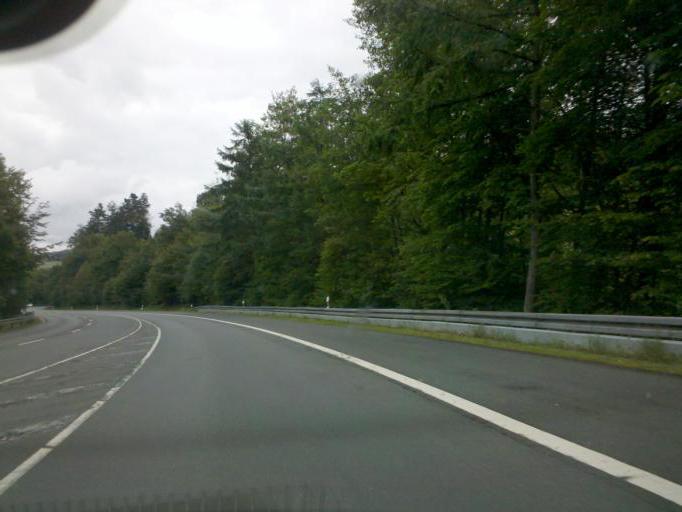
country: DE
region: North Rhine-Westphalia
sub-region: Regierungsbezirk Arnsberg
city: Meschede
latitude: 51.3723
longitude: 8.2930
